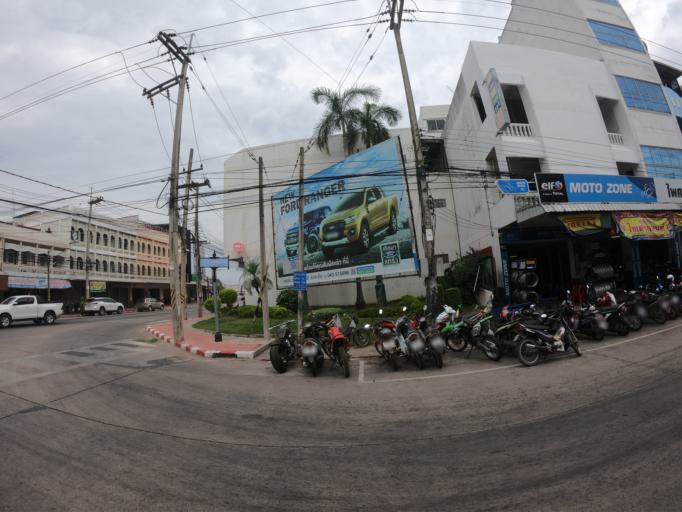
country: TH
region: Roi Et
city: Roi Et
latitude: 16.0603
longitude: 103.6569
